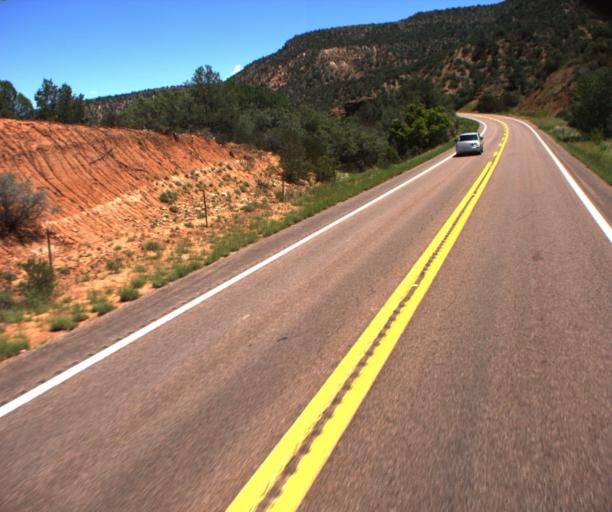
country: US
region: Arizona
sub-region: Navajo County
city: Cibecue
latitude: 34.0125
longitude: -110.2466
